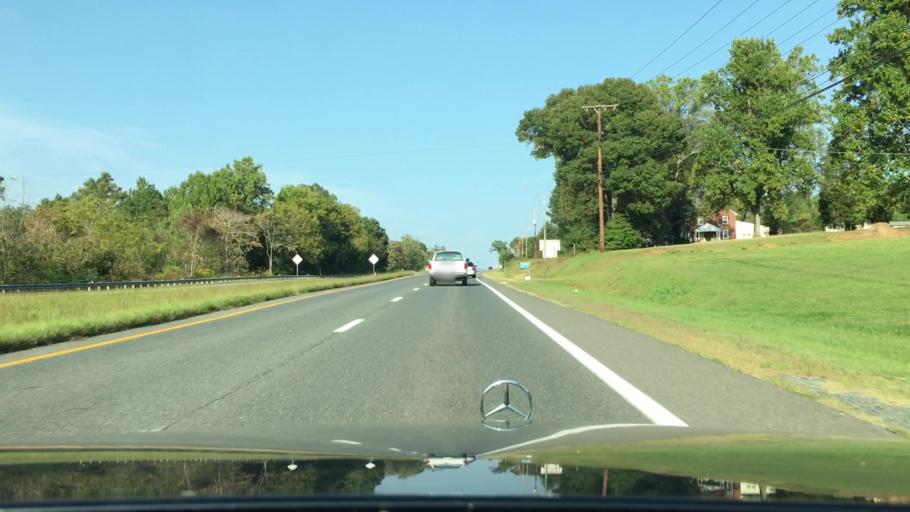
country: US
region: Virginia
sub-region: Amherst County
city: Amherst
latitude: 37.5255
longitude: -79.1116
